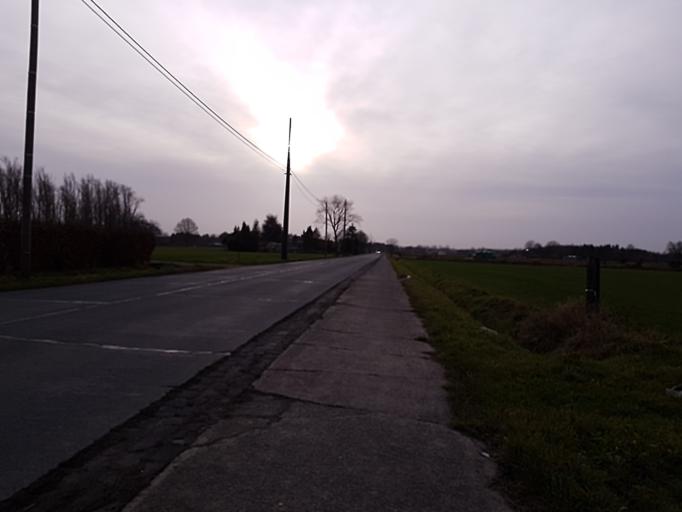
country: BE
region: Flanders
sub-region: Provincie Antwerpen
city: Putte
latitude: 51.0428
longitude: 4.6784
